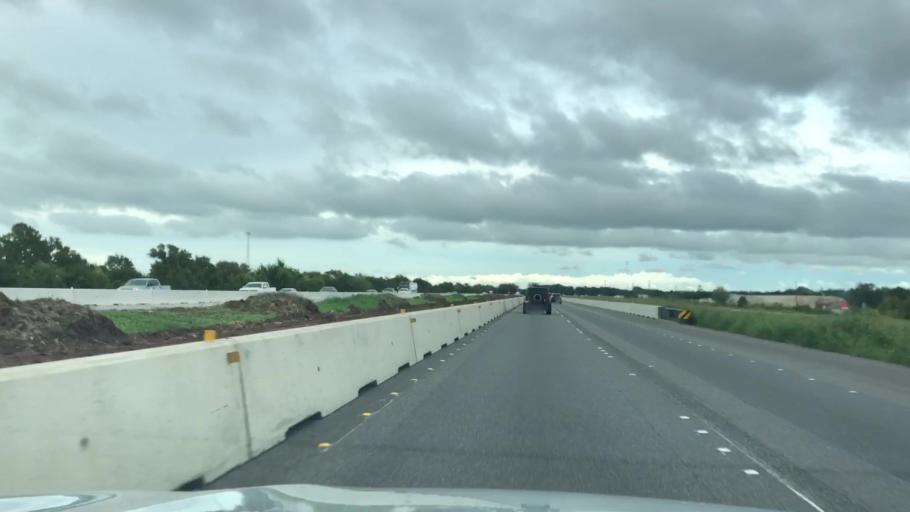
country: US
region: Texas
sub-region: Waller County
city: Brookshire
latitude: 29.7792
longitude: -96.0022
